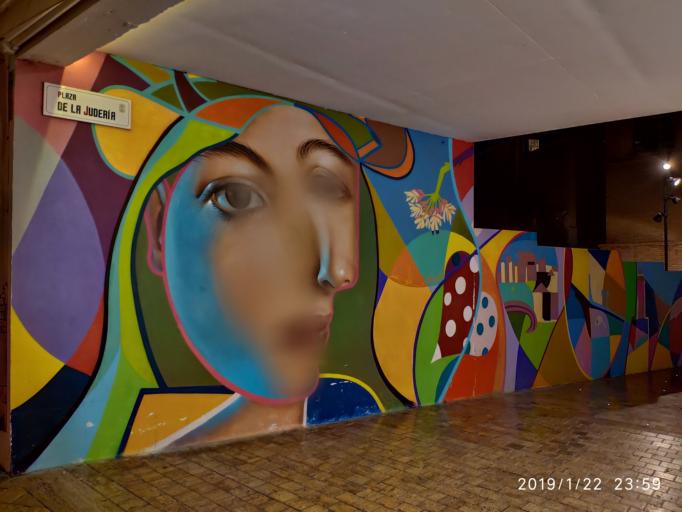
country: ES
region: Andalusia
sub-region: Provincia de Malaga
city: Malaga
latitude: 36.7218
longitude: -4.4176
